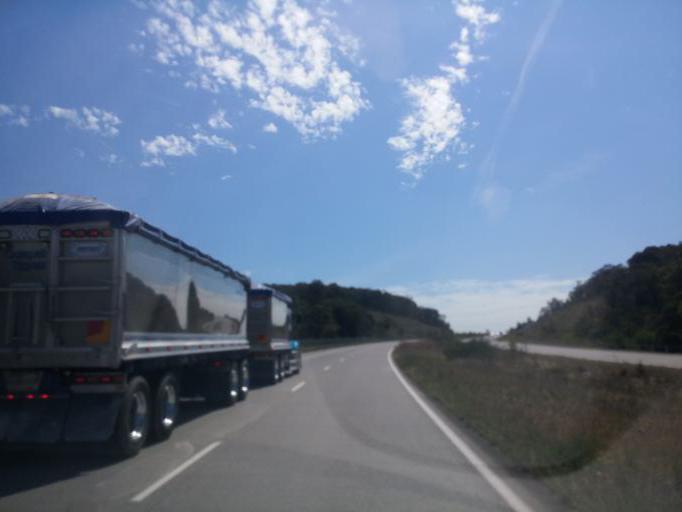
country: AU
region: New South Wales
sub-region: Great Lakes
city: Bulahdelah
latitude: -32.4809
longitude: 152.1927
